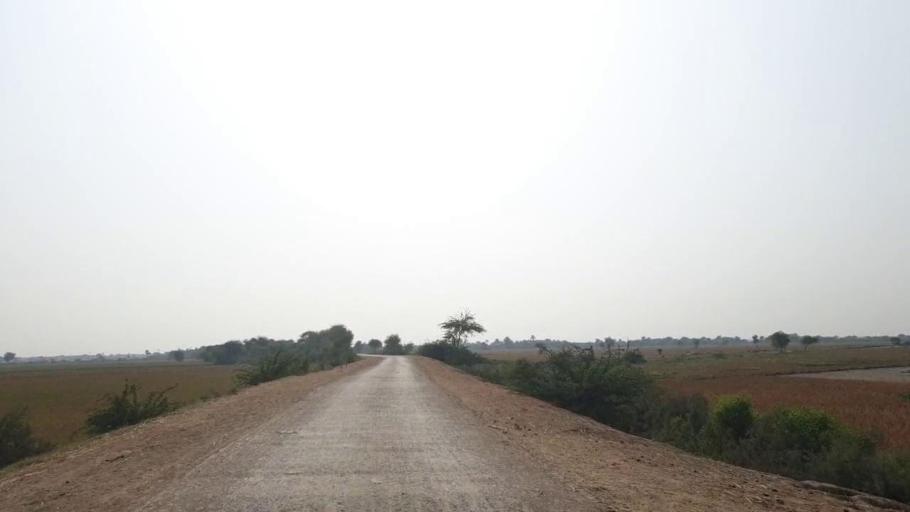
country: PK
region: Sindh
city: Matli
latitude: 24.9687
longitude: 68.5853
